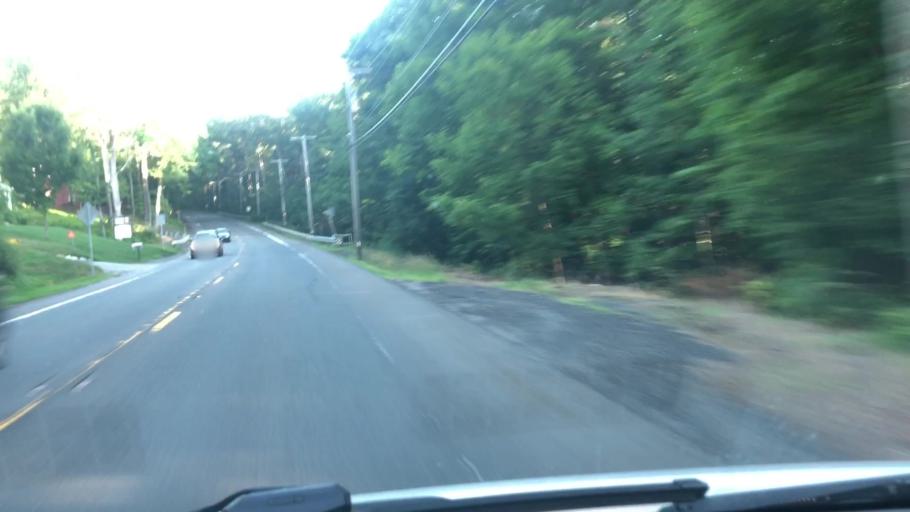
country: US
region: Massachusetts
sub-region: Hampshire County
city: Williamsburg
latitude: 42.4144
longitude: -72.7608
